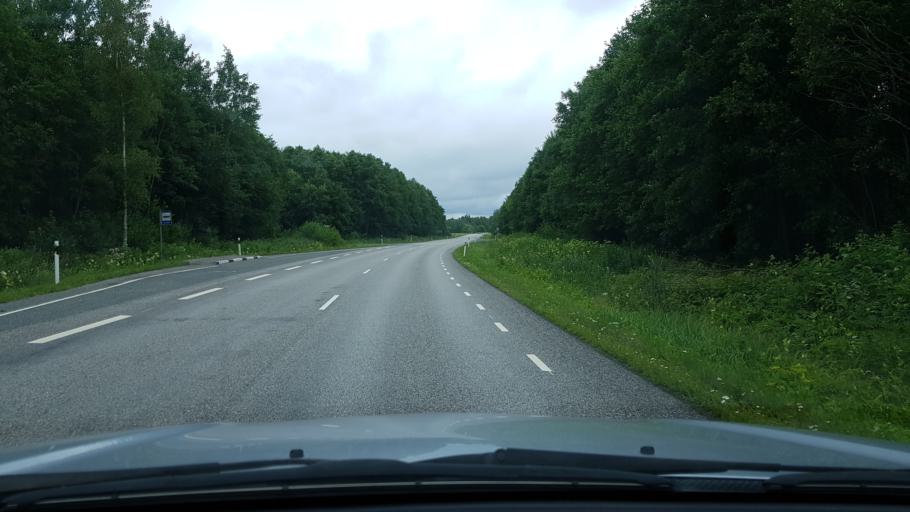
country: EE
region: Ida-Virumaa
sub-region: Narva-Joesuu linn
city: Narva-Joesuu
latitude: 59.3449
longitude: 27.9332
